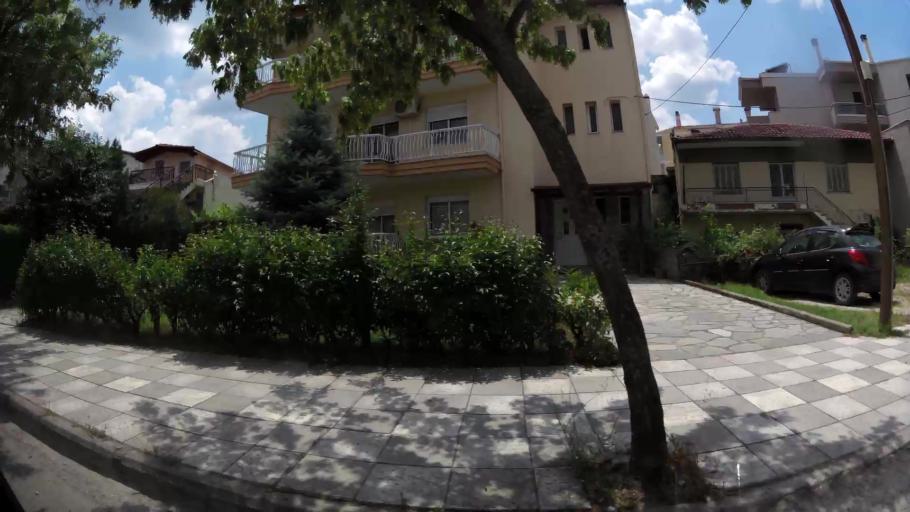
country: GR
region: West Macedonia
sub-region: Nomos Kozanis
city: Kozani
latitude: 40.2939
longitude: 21.7879
